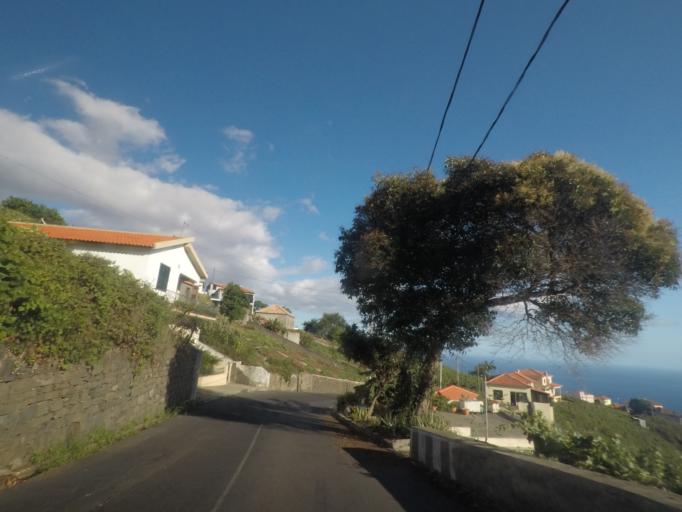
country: PT
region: Madeira
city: Camara de Lobos
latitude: 32.6680
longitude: -16.9801
